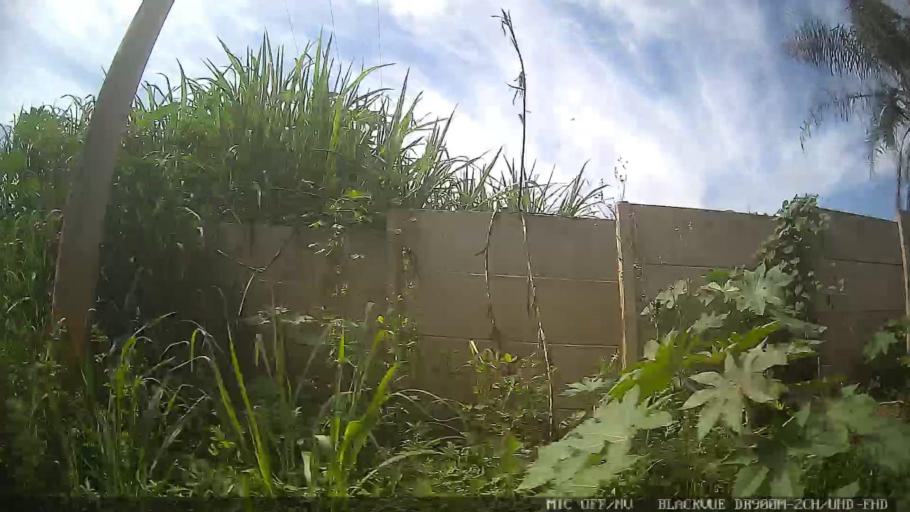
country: BR
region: Sao Paulo
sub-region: Jarinu
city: Jarinu
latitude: -23.0501
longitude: -46.6420
